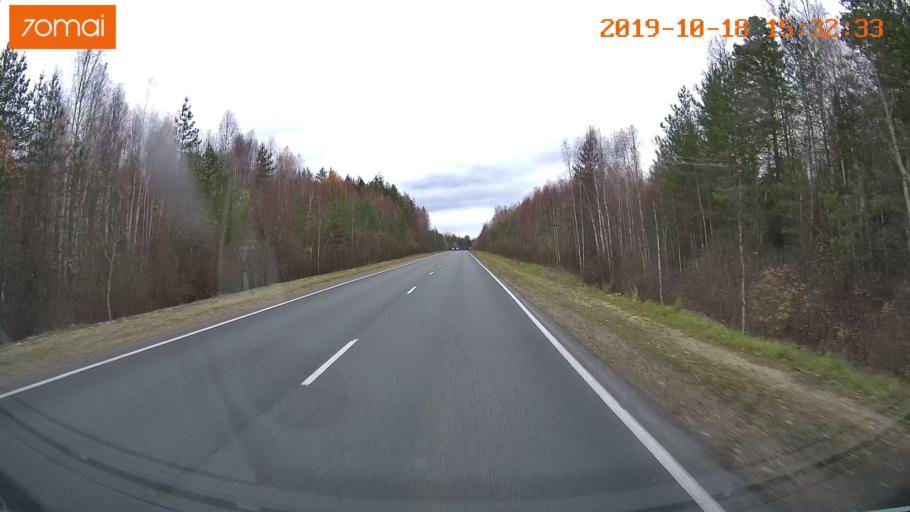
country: RU
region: Vladimir
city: Anopino
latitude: 55.8278
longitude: 40.6514
